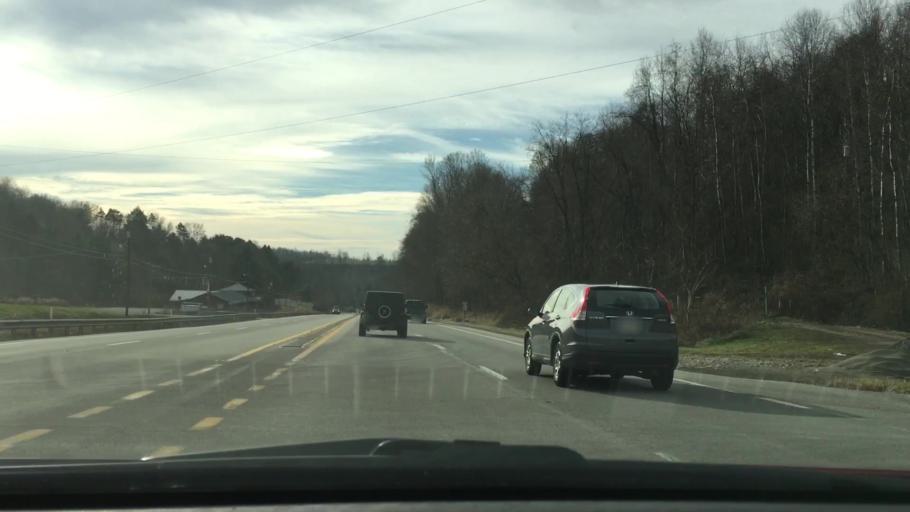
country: US
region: Pennsylvania
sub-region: Fayette County
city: Perryopolis
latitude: 40.0193
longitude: -79.7654
